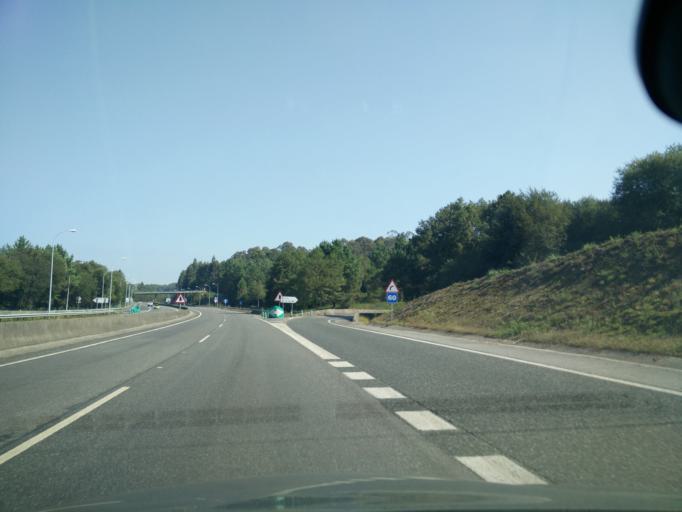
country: ES
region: Galicia
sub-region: Provincia da Coruna
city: Mino
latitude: 43.3744
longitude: -8.1852
